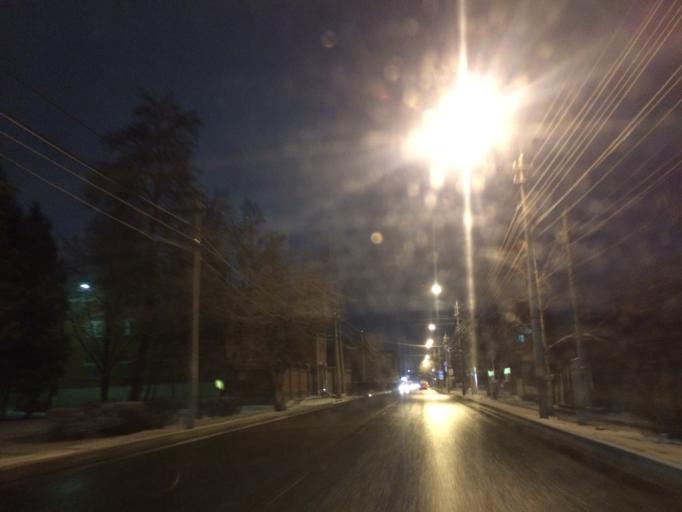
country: RU
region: Tula
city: Tula
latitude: 54.1865
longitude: 37.6268
